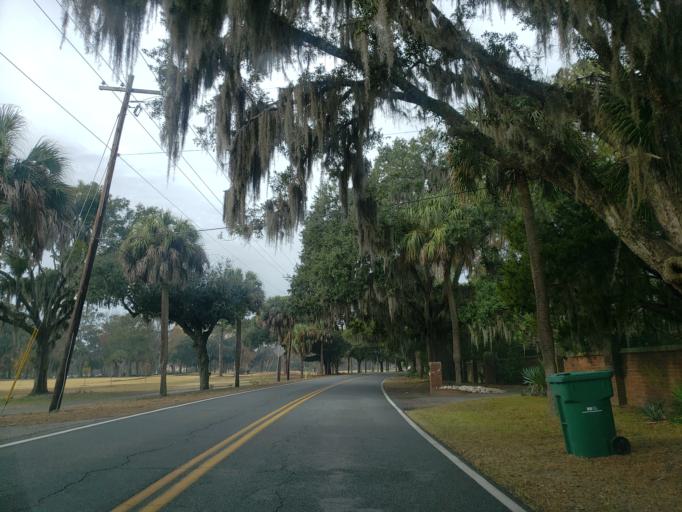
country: US
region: Georgia
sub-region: Chatham County
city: Wilmington Island
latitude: 32.0055
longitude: -80.9909
